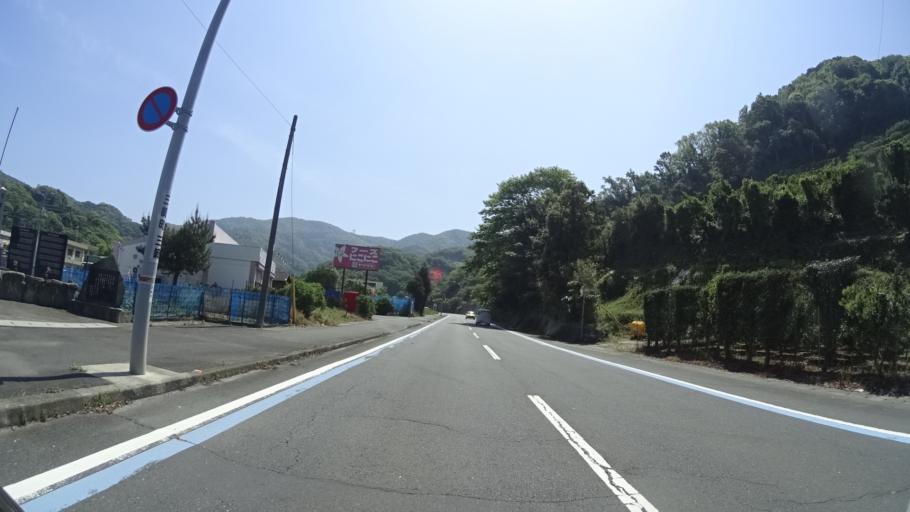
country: JP
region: Ehime
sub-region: Nishiuwa-gun
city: Ikata-cho
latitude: 33.3869
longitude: 132.1239
